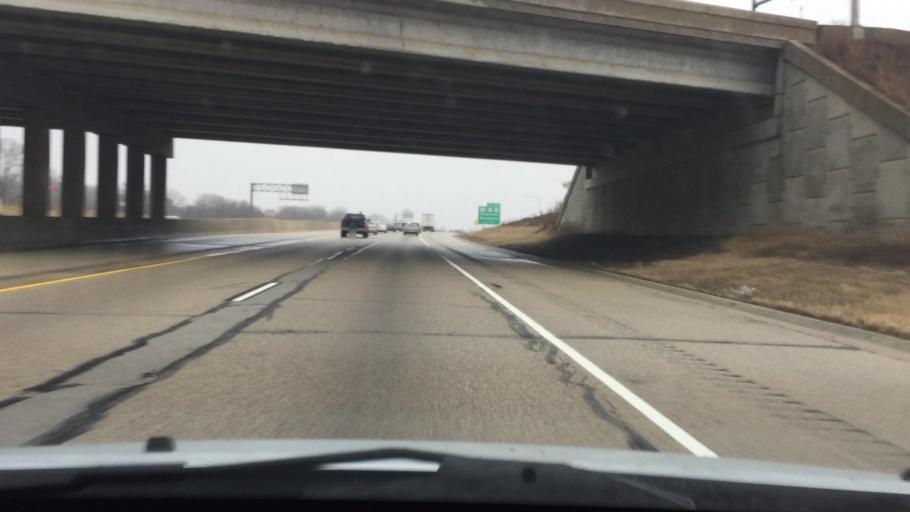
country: US
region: Wisconsin
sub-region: Waukesha County
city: Pewaukee
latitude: 43.0506
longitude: -88.3036
